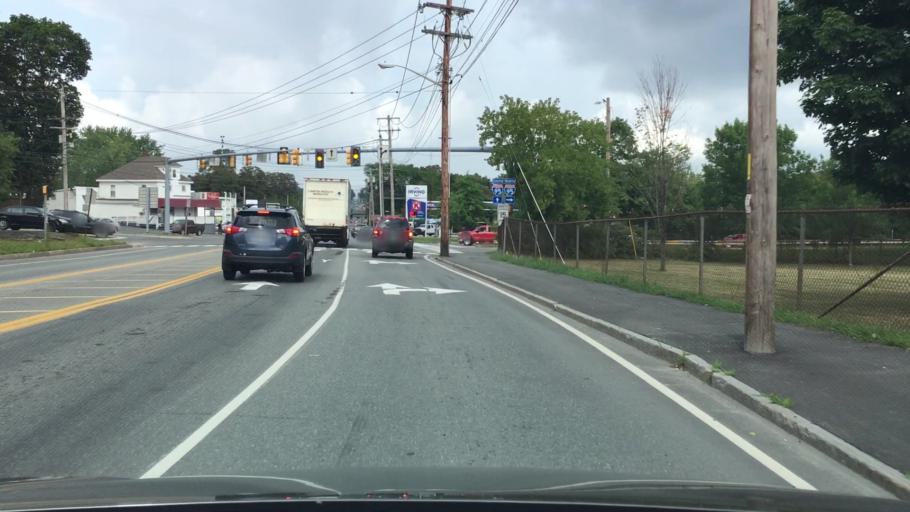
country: US
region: Maine
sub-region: Penobscot County
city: Bangor
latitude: 44.8173
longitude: -68.7734
